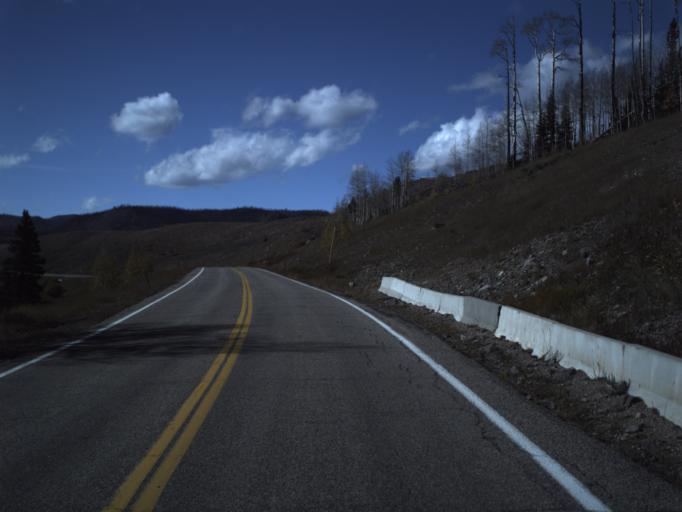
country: US
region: Utah
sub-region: Iron County
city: Parowan
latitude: 37.6634
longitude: -112.7183
